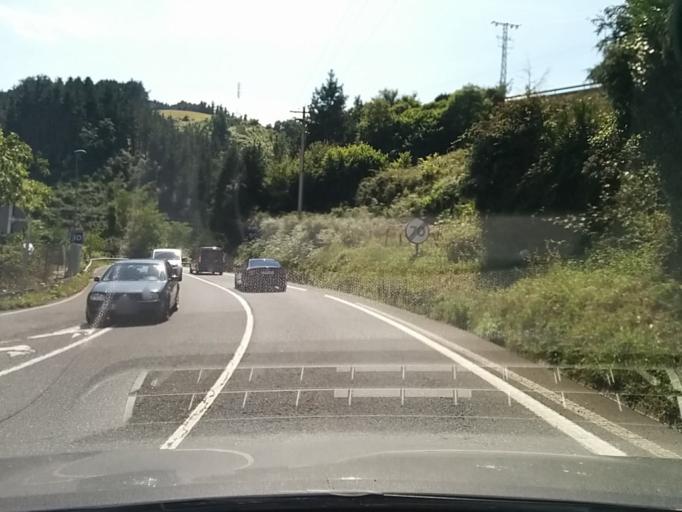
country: ES
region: Basque Country
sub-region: Provincia de Guipuzcoa
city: Mutriku
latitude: 43.3073
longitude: -2.3918
